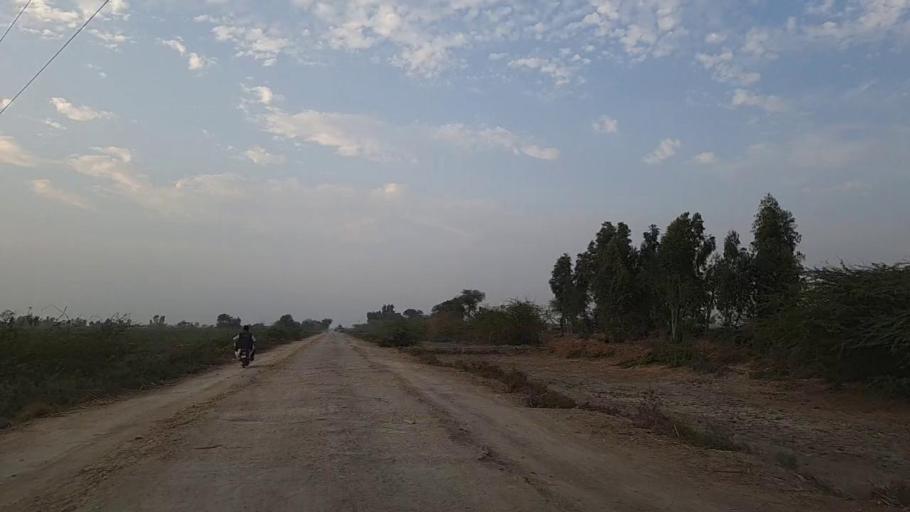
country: PK
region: Sindh
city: Mirwah Gorchani
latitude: 25.3154
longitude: 69.2229
